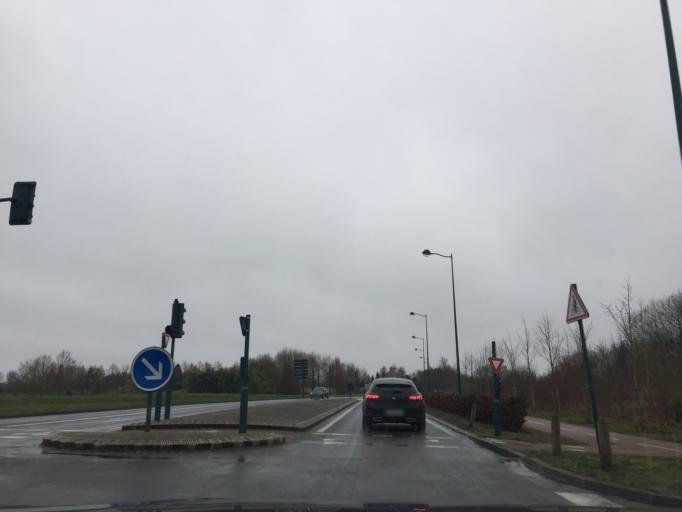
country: FR
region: Ile-de-France
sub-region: Departement de Seine-et-Marne
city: Magny-le-Hongre
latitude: 48.8618
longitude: 2.8070
